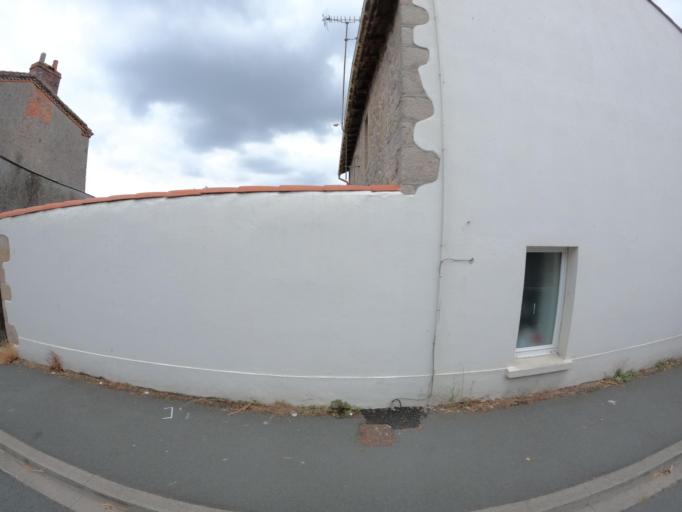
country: FR
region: Pays de la Loire
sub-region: Departement de Maine-et-Loire
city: Le Longeron
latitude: 47.0176
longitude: -1.0623
